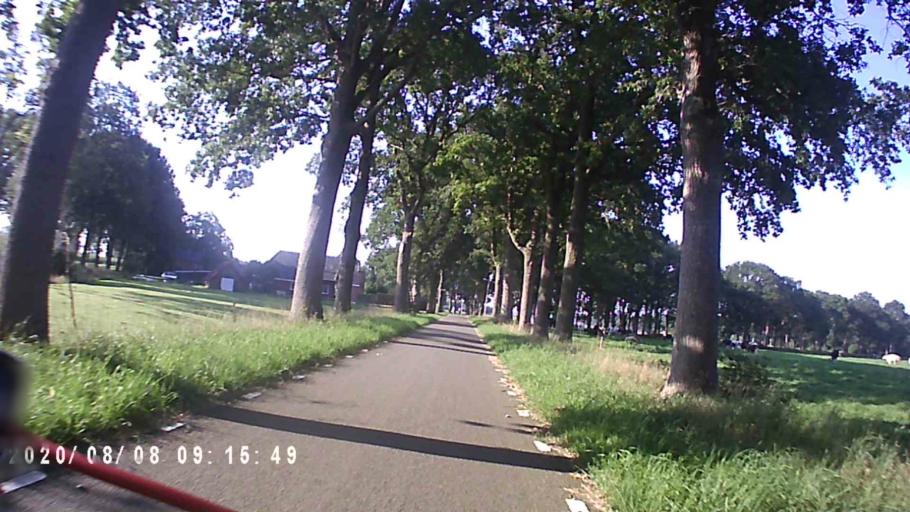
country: NL
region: Groningen
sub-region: Gemeente Leek
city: Leek
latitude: 53.0424
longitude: 6.3303
